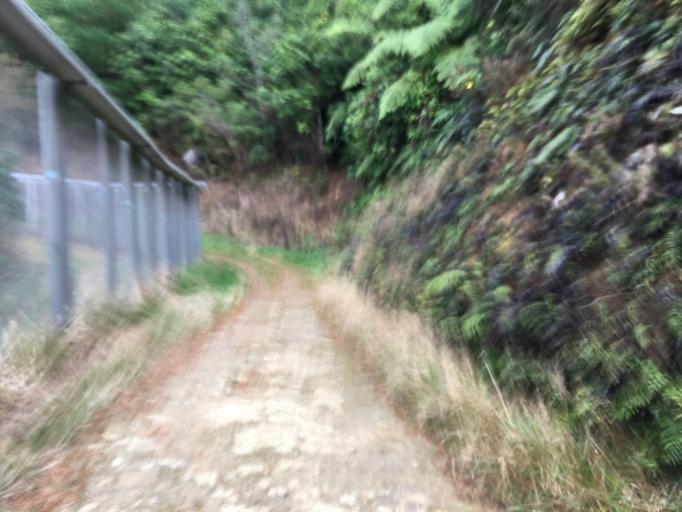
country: NZ
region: Wellington
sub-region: Wellington City
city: Brooklyn
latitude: -41.2988
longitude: 174.7387
